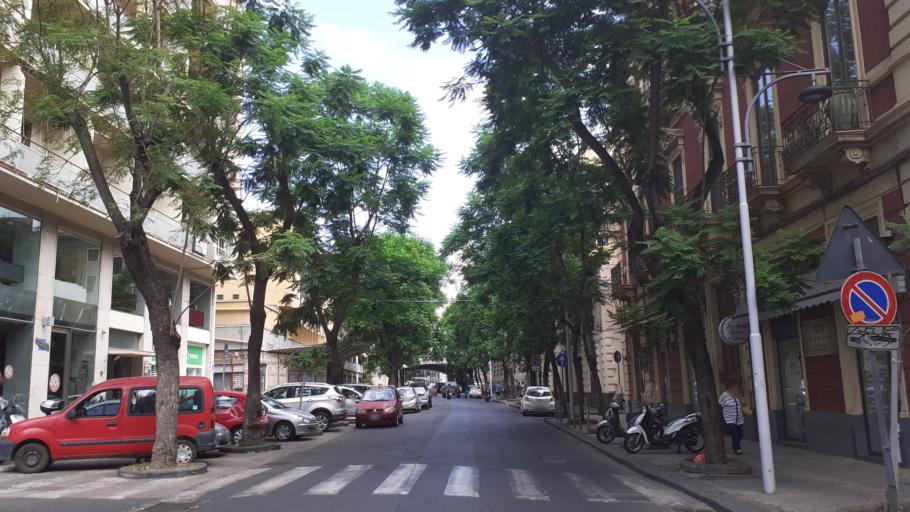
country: IT
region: Sicily
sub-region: Catania
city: Catania
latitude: 37.5093
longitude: 15.0849
